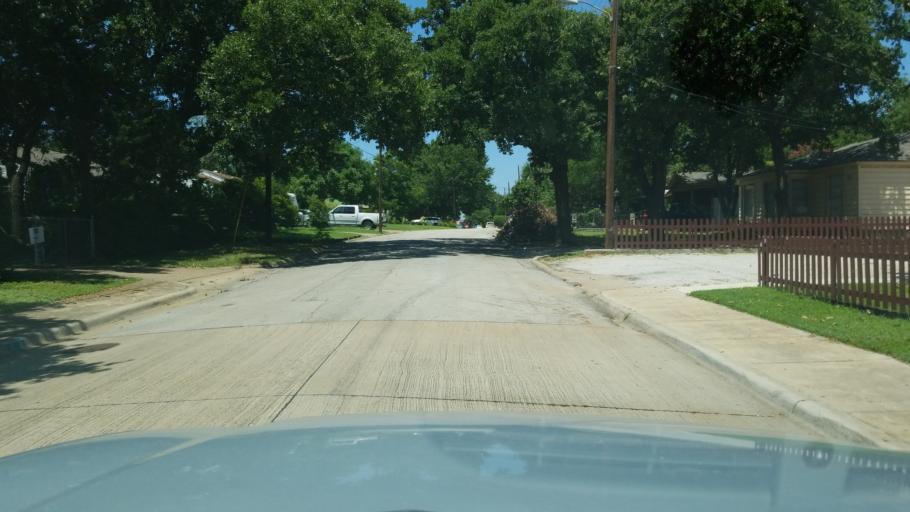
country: US
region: Texas
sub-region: Dallas County
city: Irving
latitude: 32.8072
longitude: -96.9175
